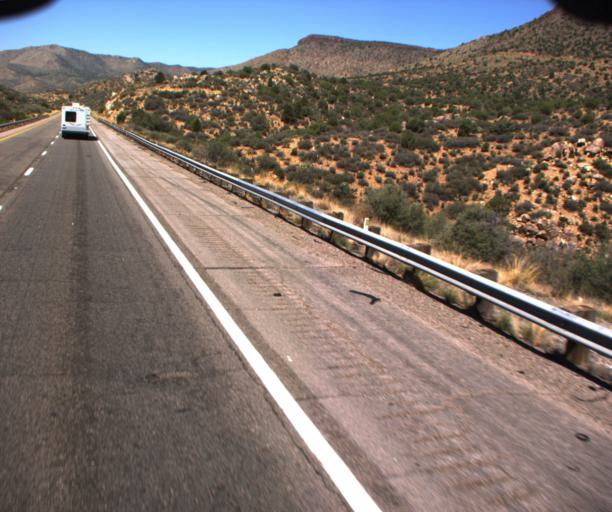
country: US
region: Arizona
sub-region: Mohave County
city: Peach Springs
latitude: 35.1790
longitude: -113.4882
